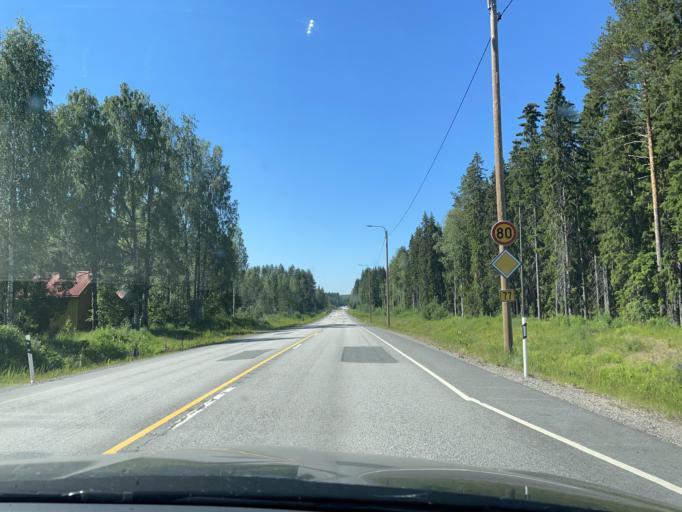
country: FI
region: Central Finland
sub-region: Saarijaervi-Viitasaari
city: Viitasaari
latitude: 63.1725
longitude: 26.0114
